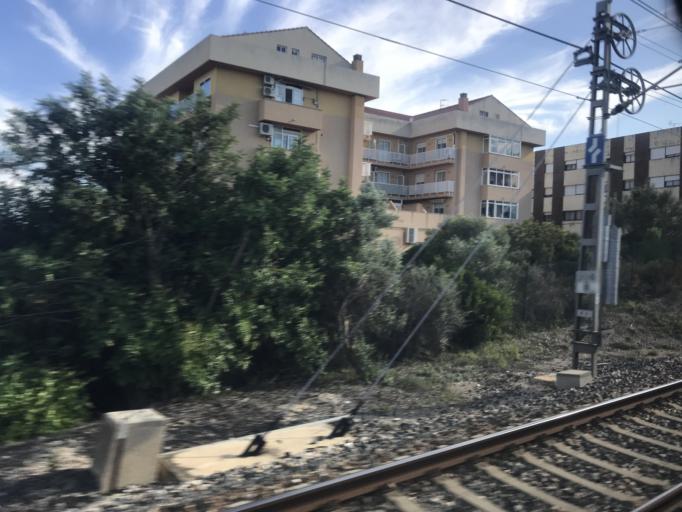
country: ES
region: Catalonia
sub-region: Provincia de Tarragona
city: l'Ametlla de Mar
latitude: 40.8826
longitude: 0.7972
